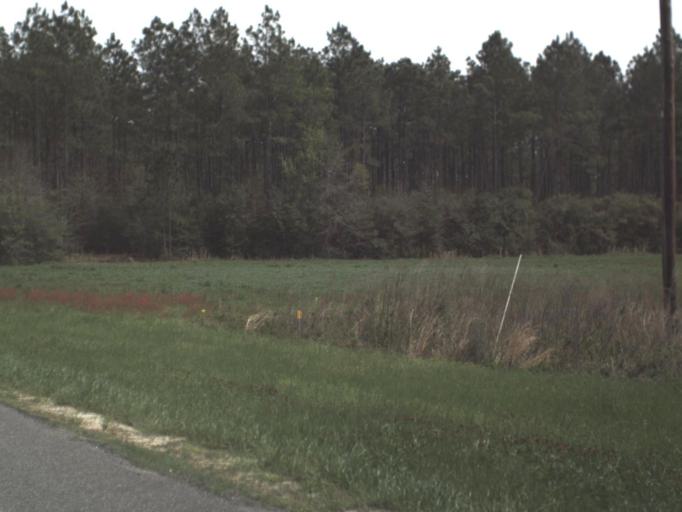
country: US
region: Alabama
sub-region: Geneva County
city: Geneva
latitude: 30.9566
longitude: -85.9047
